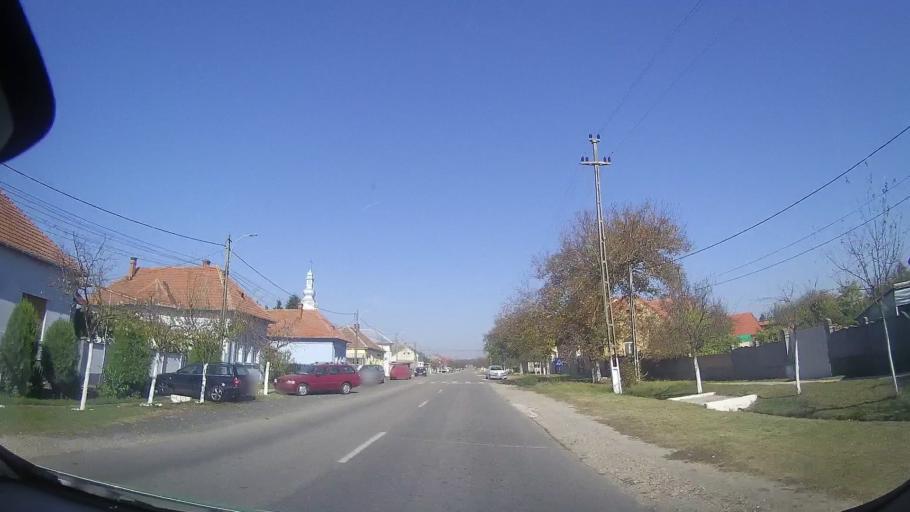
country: RO
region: Timis
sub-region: Comuna Costeiu
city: Costeiu
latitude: 45.7418
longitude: 21.8484
